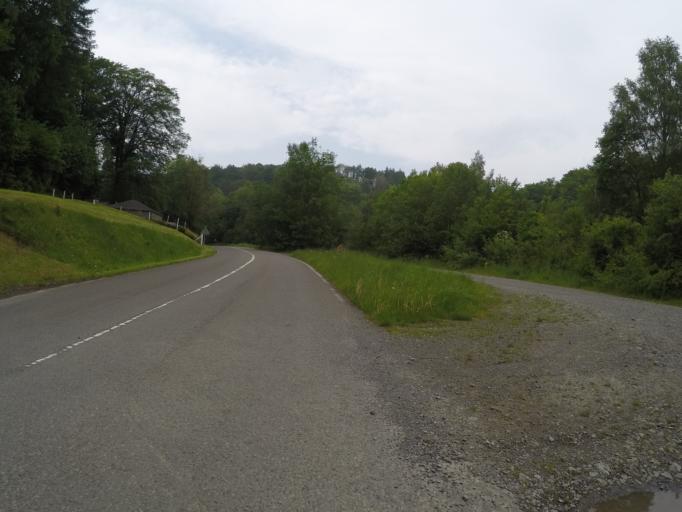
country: BE
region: Wallonia
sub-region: Province de Namur
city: Assesse
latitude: 50.3289
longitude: 5.0039
